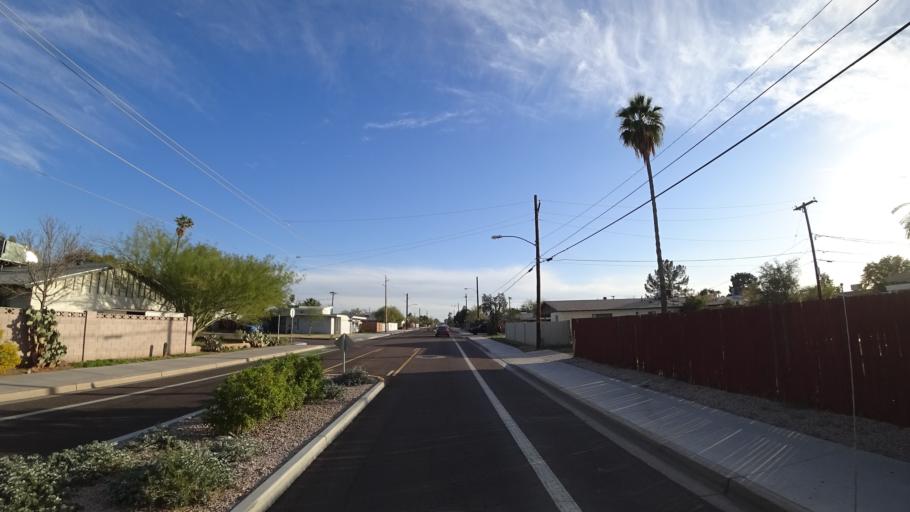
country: US
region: Arizona
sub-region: Maricopa County
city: Tempe Junction
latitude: 33.4195
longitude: -111.9522
